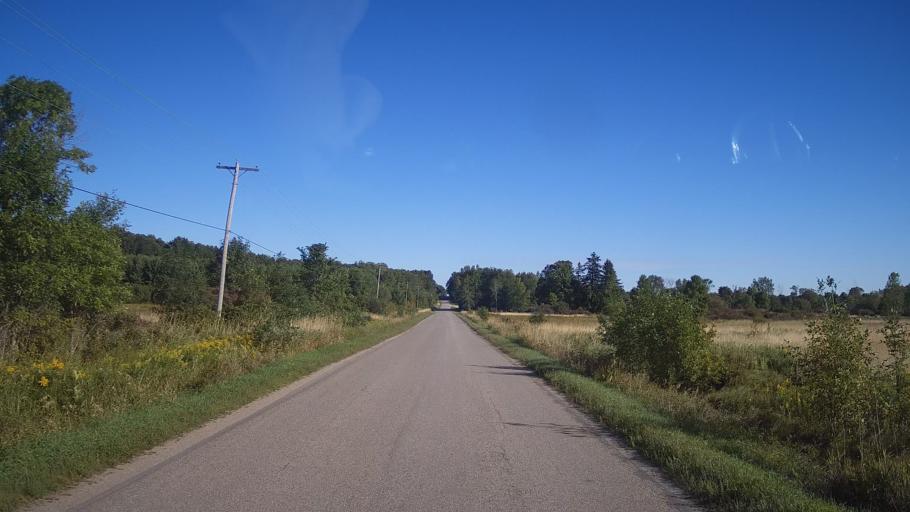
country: US
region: New York
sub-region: Jefferson County
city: Alexandria Bay
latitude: 44.4379
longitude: -75.9824
